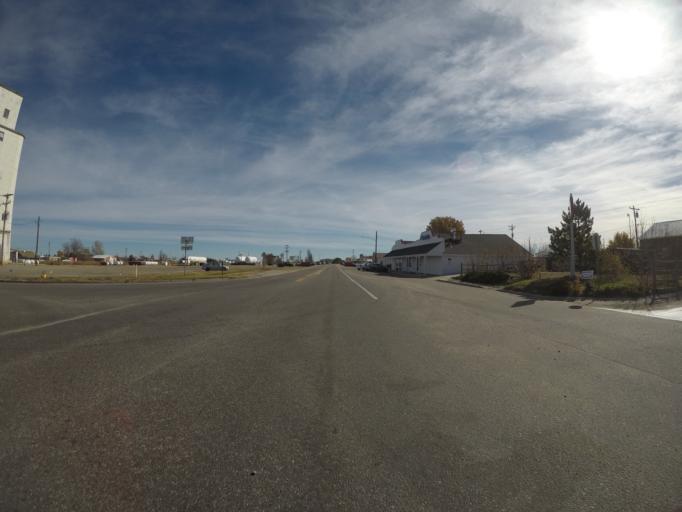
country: US
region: Colorado
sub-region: Adams County
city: Bennett
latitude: 39.7558
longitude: -104.4275
